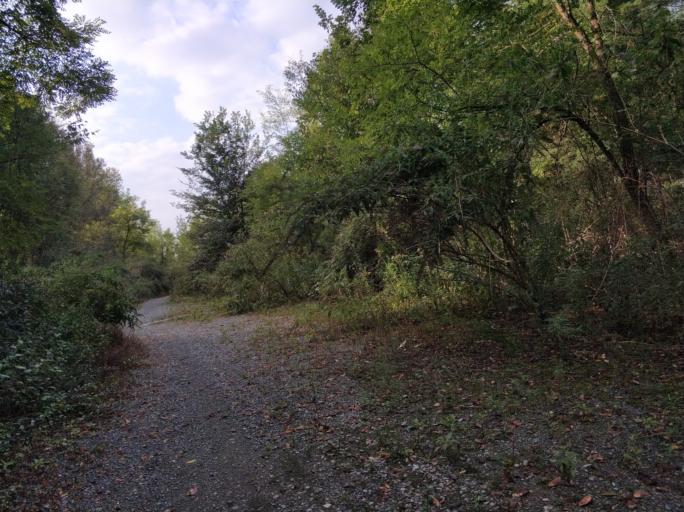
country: IT
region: Piedmont
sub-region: Provincia di Torino
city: Robassomero
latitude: 45.2130
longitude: 7.5691
